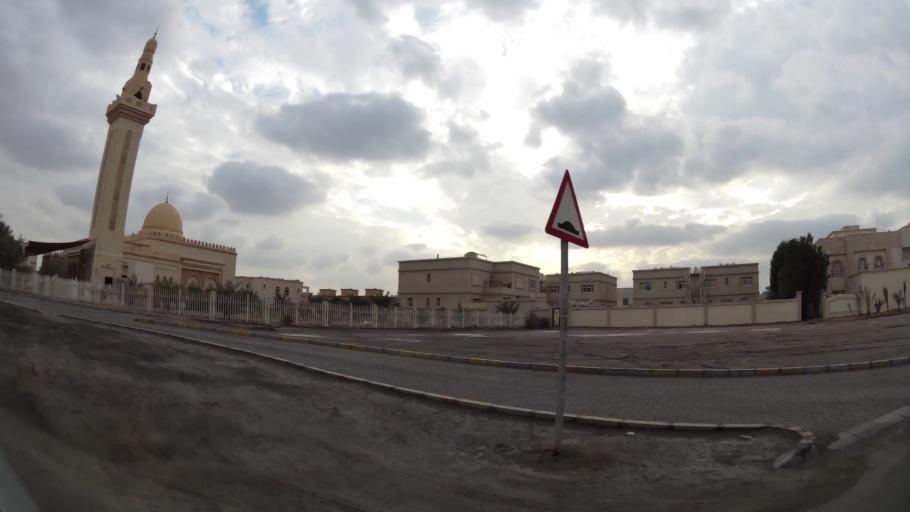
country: AE
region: Abu Dhabi
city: Abu Dhabi
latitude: 24.3542
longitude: 54.5459
